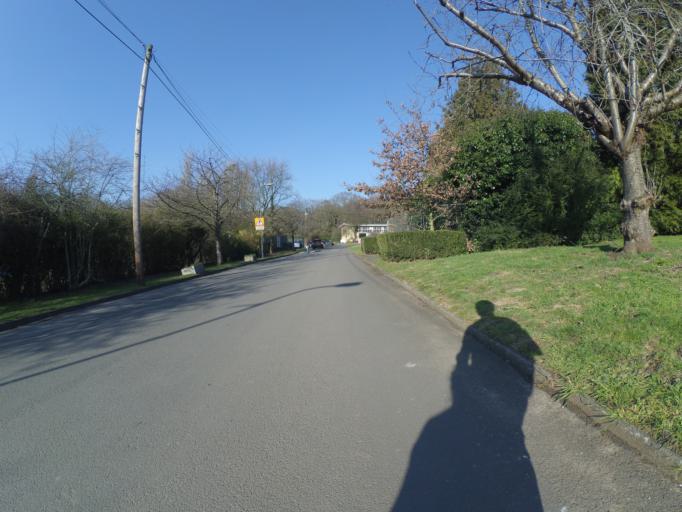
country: GB
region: England
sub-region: Greater London
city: Wembley
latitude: 51.5700
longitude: -0.2583
